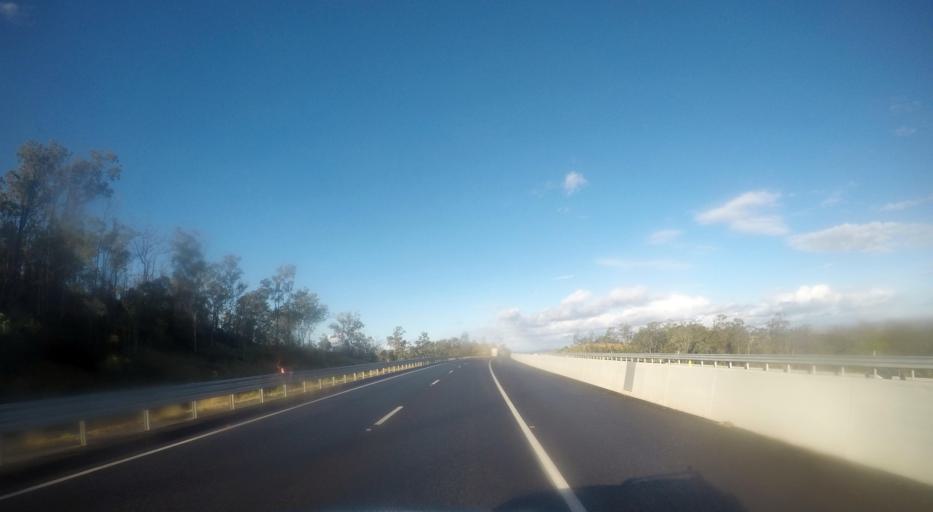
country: AU
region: Queensland
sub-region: Toowoomba
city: East Toowoomba
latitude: -27.5143
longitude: 152.0428
